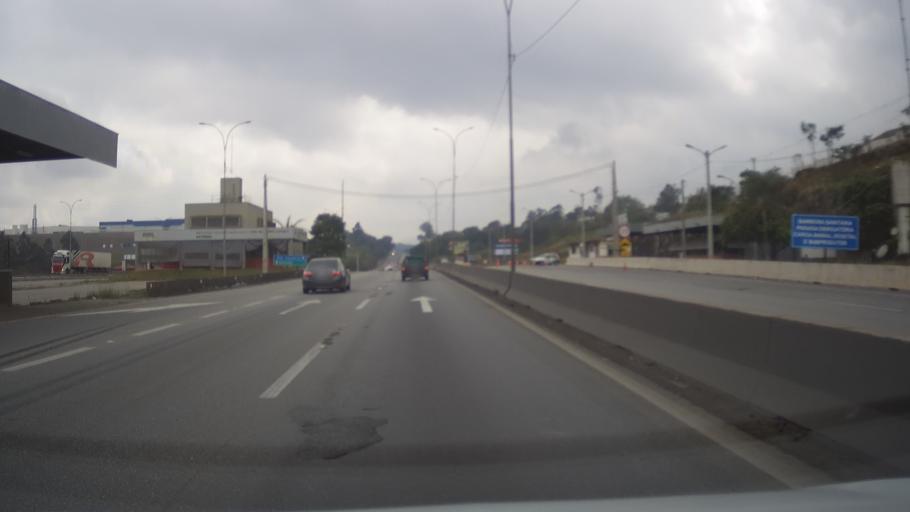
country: BR
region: Minas Gerais
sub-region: Extrema
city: Extrema
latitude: -22.8719
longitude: -46.3608
